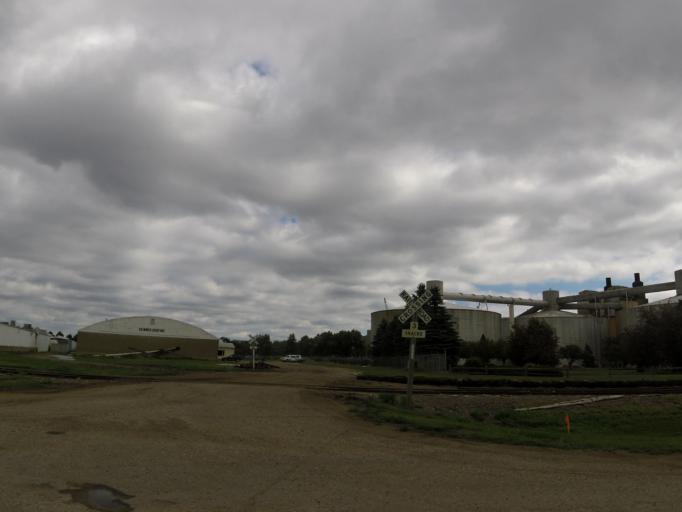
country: US
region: Minnesota
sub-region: Polk County
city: East Grand Forks
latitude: 47.9249
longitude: -97.0093
